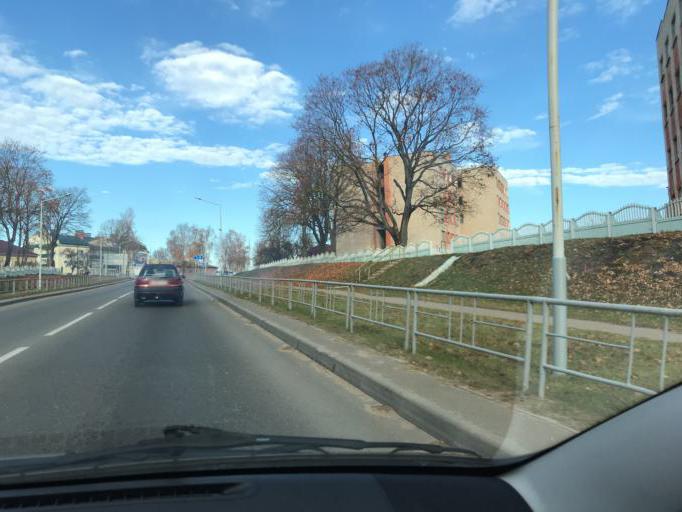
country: BY
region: Vitebsk
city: Haradok
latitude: 55.4701
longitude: 29.9716
